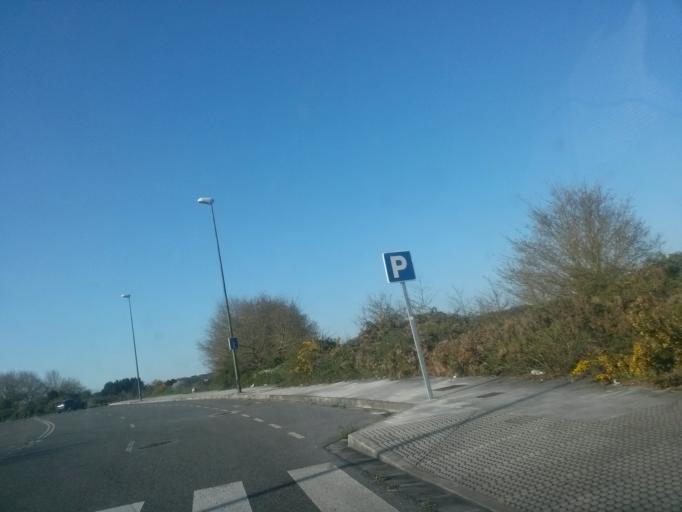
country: ES
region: Galicia
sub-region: Provincia de Lugo
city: Lugo
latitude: 42.9987
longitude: -7.5383
